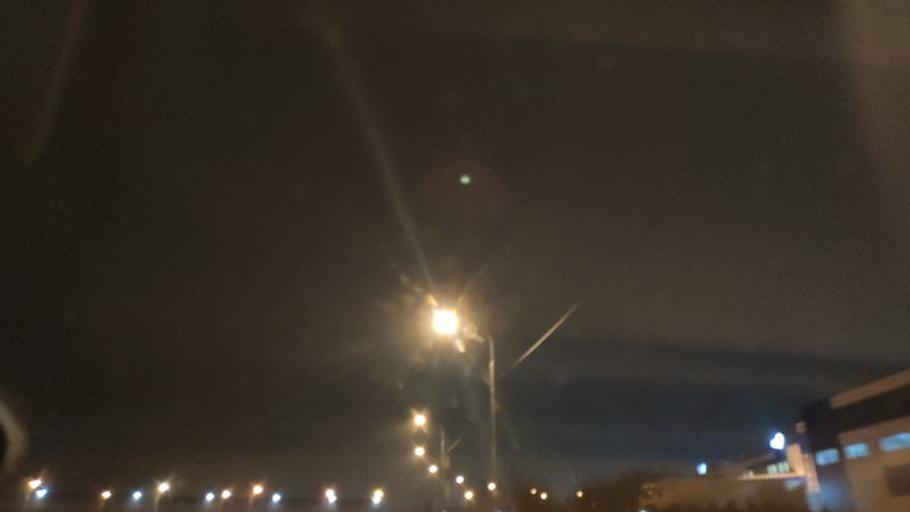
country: RU
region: Moskovskaya
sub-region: Podol'skiy Rayon
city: Podol'sk
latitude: 55.4380
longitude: 37.6112
